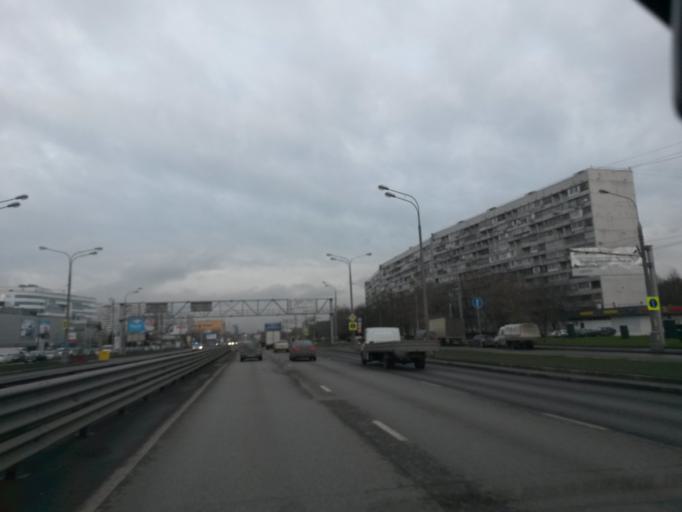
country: RU
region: Moscow
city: Chertanovo Yuzhnoye
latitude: 55.5975
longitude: 37.6035
